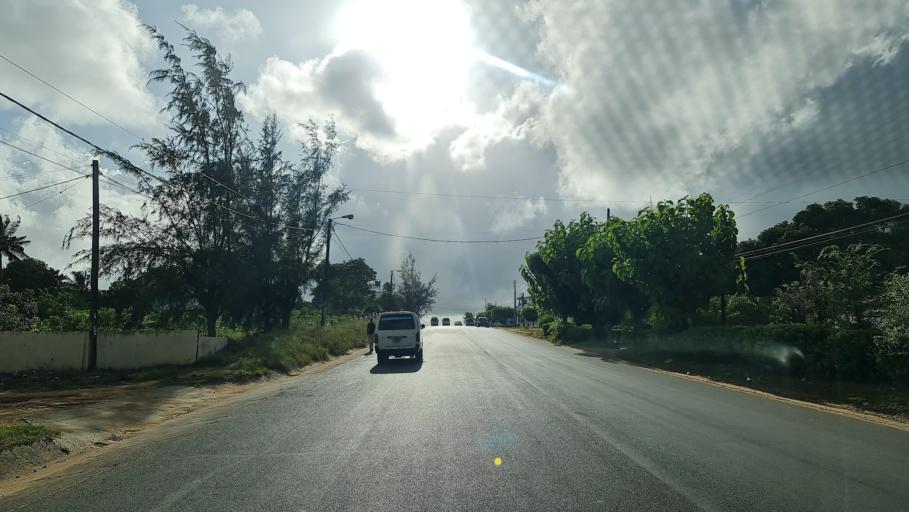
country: MZ
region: Gaza
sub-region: Xai-Xai District
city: Xai-Xai
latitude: -25.0569
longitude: 33.6594
